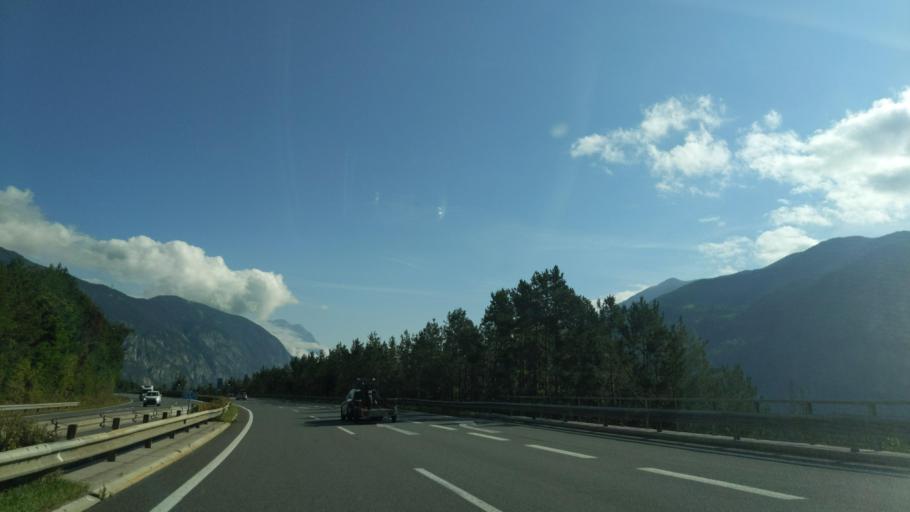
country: AT
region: Tyrol
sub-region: Politischer Bezirk Imst
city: Roppen
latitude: 47.2366
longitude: 10.8425
